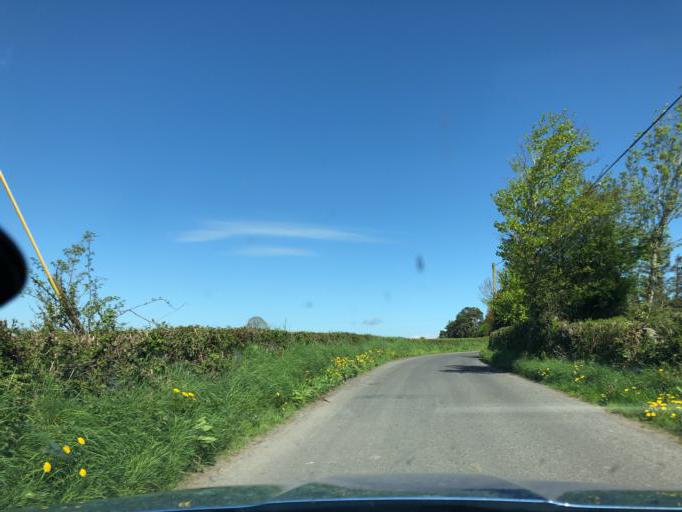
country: IE
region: Connaught
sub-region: County Galway
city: Portumna
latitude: 53.1504
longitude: -8.2926
